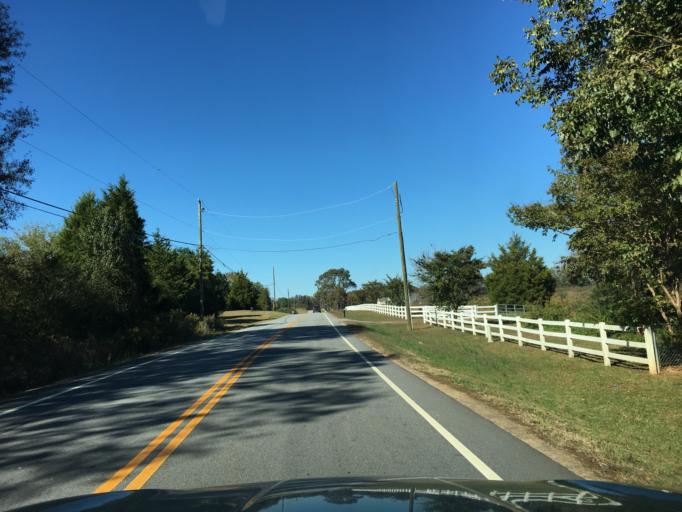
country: US
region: South Carolina
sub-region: Spartanburg County
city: Wellford
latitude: 34.8700
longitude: -82.0982
